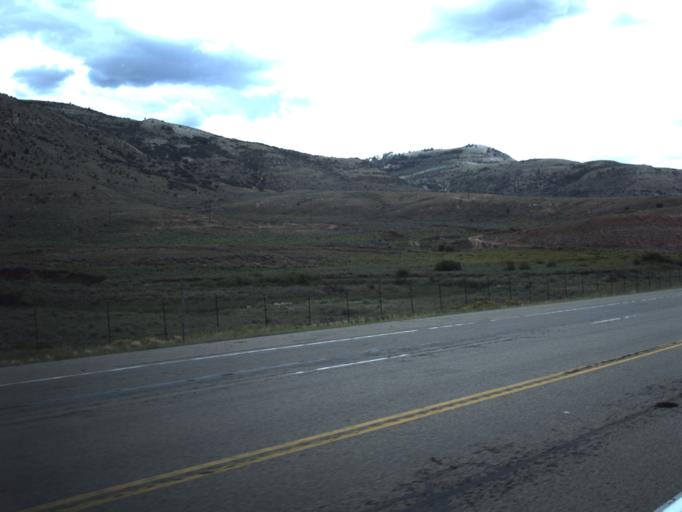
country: US
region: Utah
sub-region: Carbon County
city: Helper
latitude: 39.8777
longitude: -111.0394
